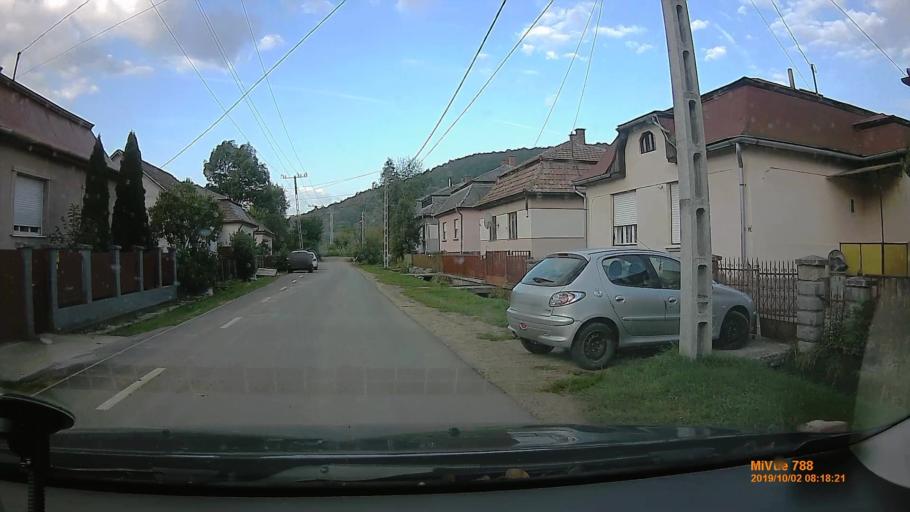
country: HU
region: Nograd
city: Matraverebely
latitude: 47.9715
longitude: 19.7707
